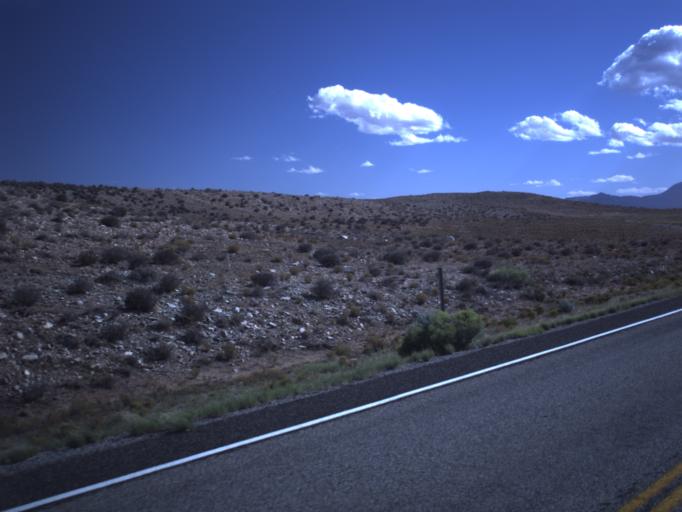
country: US
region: Utah
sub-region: Wayne County
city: Loa
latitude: 38.1184
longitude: -110.6226
